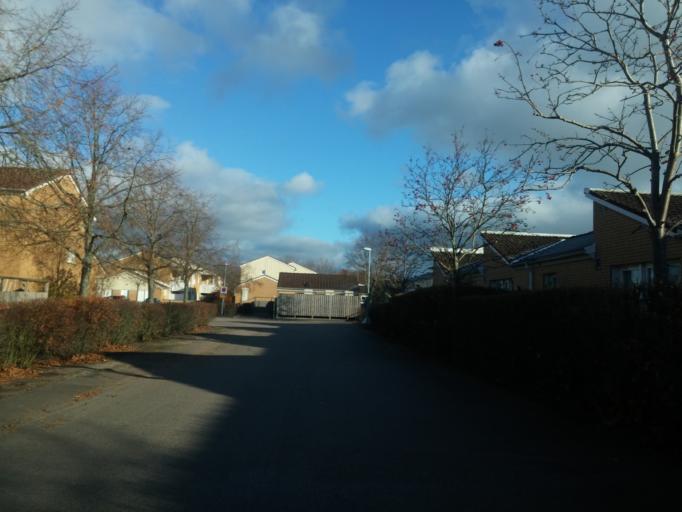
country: SE
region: Skane
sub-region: Angelholms Kommun
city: AEngelholm
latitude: 56.2254
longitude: 12.8349
